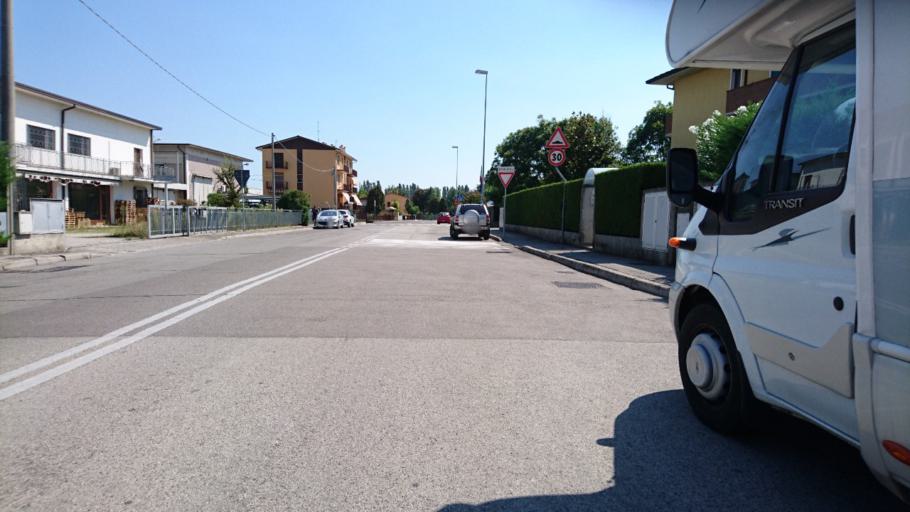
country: IT
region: Veneto
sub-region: Provincia di Padova
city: Mandriola-Sant'Agostino
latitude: 45.3683
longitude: 11.8492
